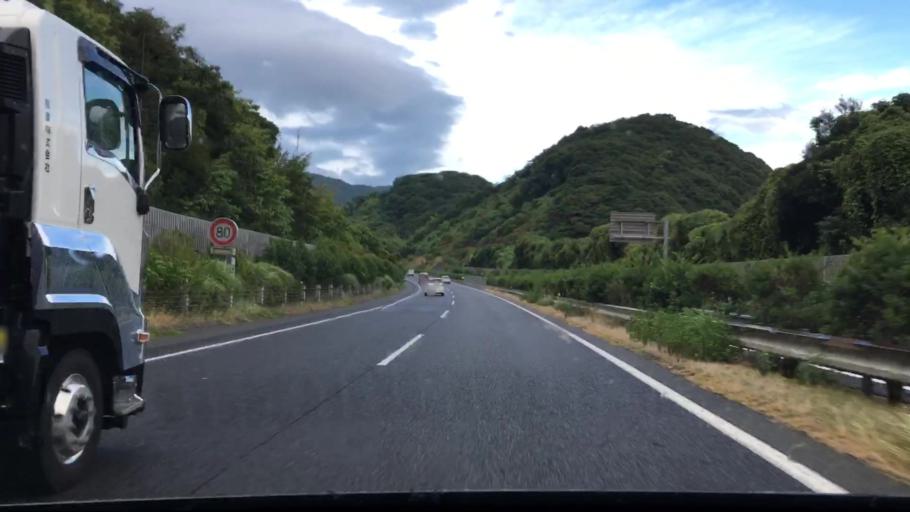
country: JP
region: Fukuoka
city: Kitakyushu
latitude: 33.8012
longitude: 130.8609
